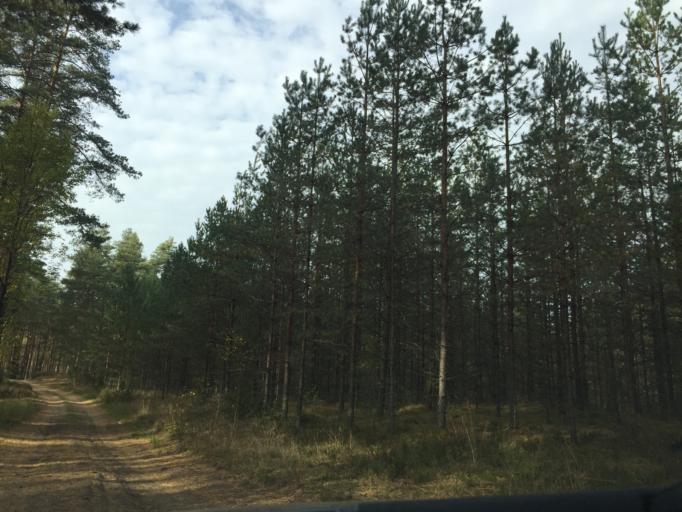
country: LV
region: Garkalne
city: Garkalne
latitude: 56.9507
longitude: 24.4285
